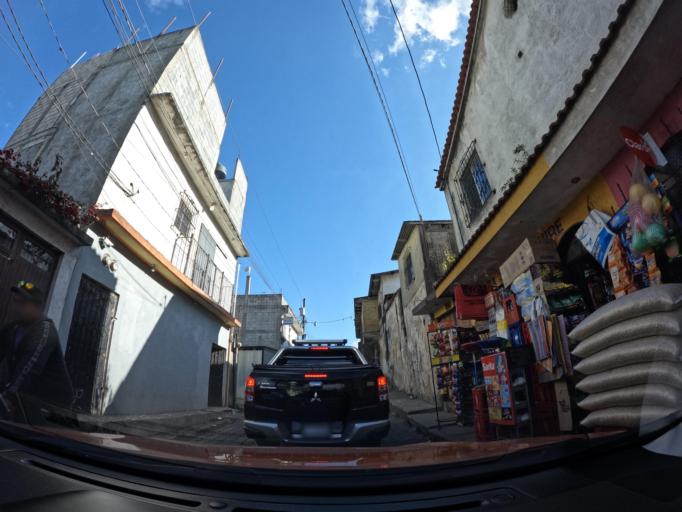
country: GT
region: Sacatepequez
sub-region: Municipio de Santa Maria de Jesus
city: Santa Maria de Jesus
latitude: 14.4944
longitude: -90.7090
